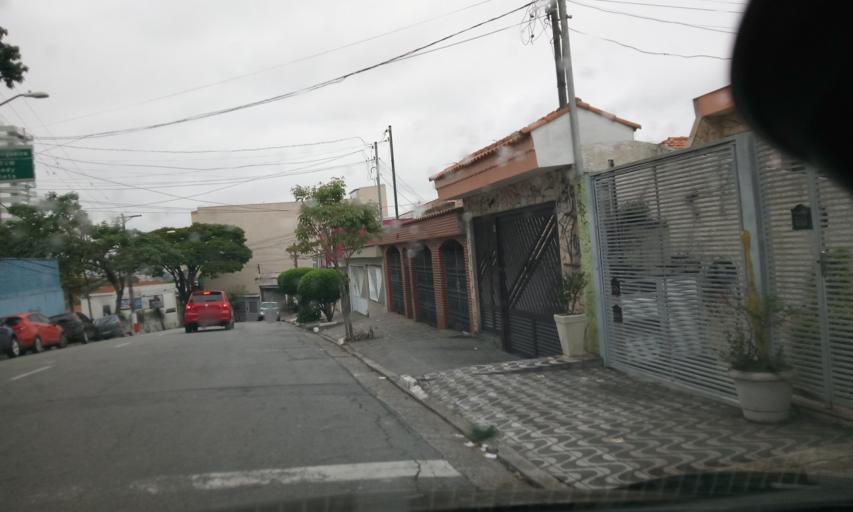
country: BR
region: Sao Paulo
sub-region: Sao Bernardo Do Campo
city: Sao Bernardo do Campo
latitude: -23.6751
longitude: -46.5621
